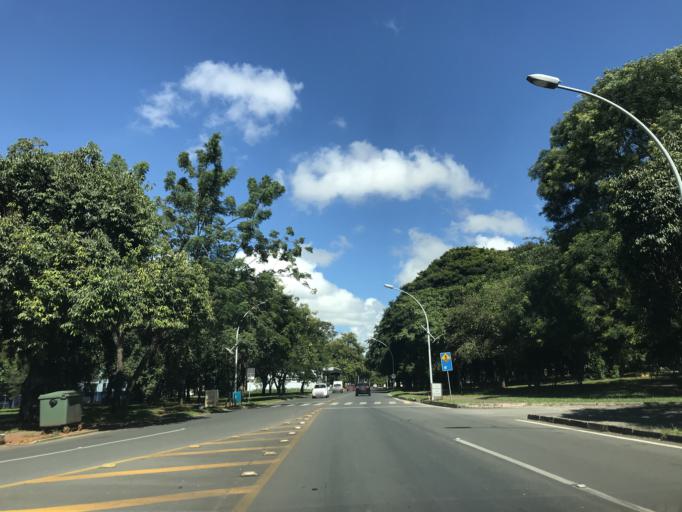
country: BR
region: Federal District
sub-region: Brasilia
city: Brasilia
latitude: -15.8220
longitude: -47.9020
